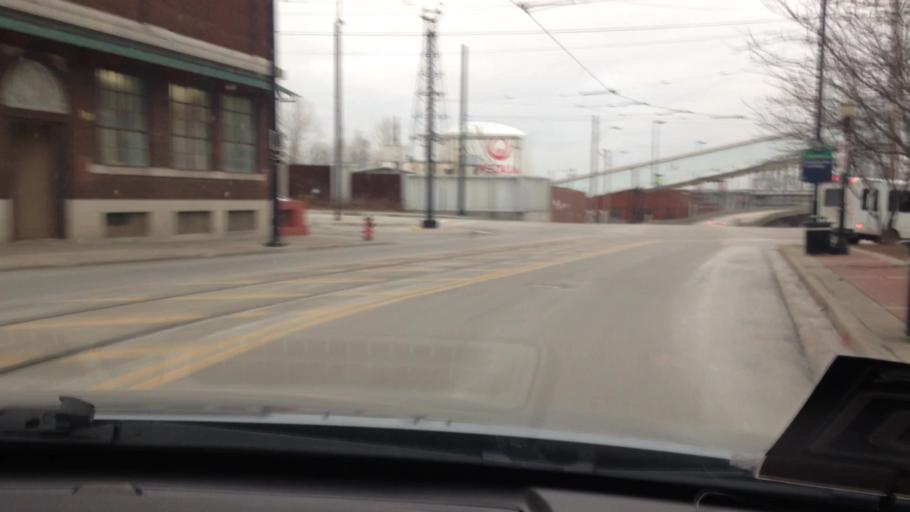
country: US
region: Missouri
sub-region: Jackson County
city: Kansas City
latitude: 39.1108
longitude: -94.5811
